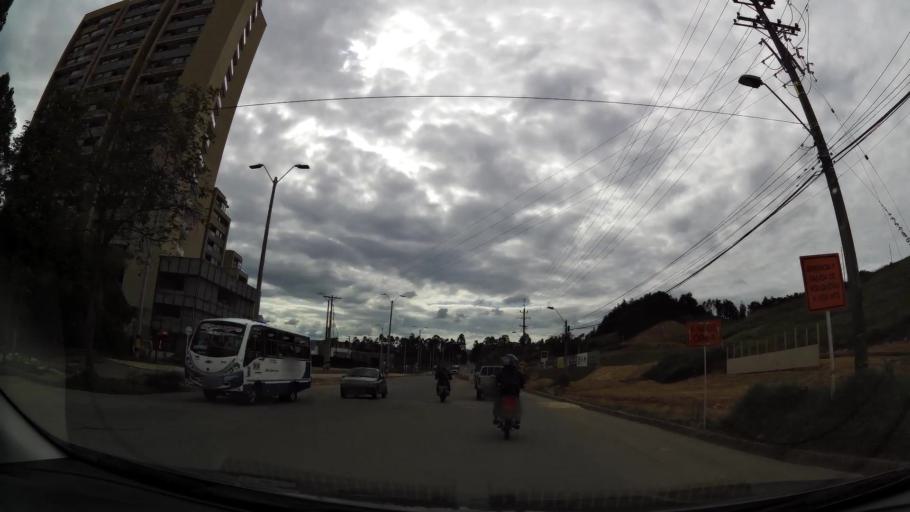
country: CO
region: Antioquia
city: Rionegro
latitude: 6.1516
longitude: -75.3964
